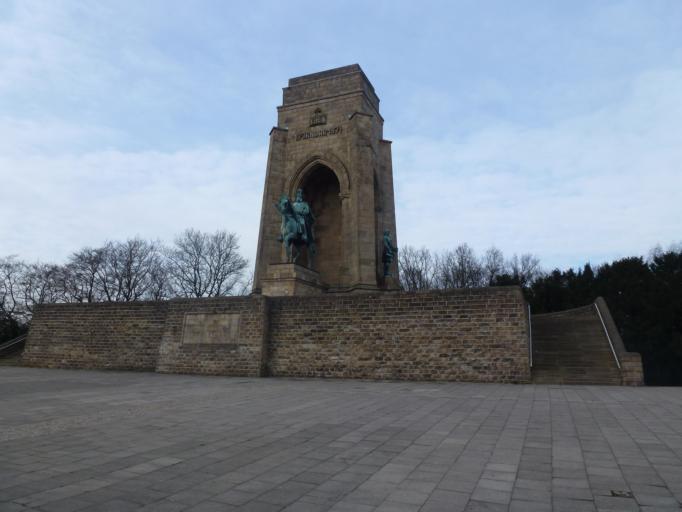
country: DE
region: North Rhine-Westphalia
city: Herdecke
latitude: 51.4197
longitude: 7.4829
